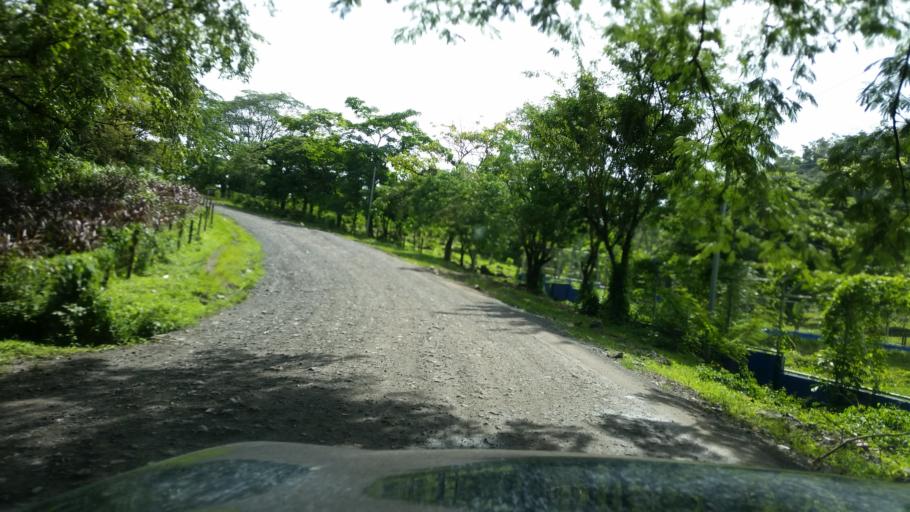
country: NI
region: Atlantico Norte (RAAN)
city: Siuna
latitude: 13.7187
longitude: -84.7648
